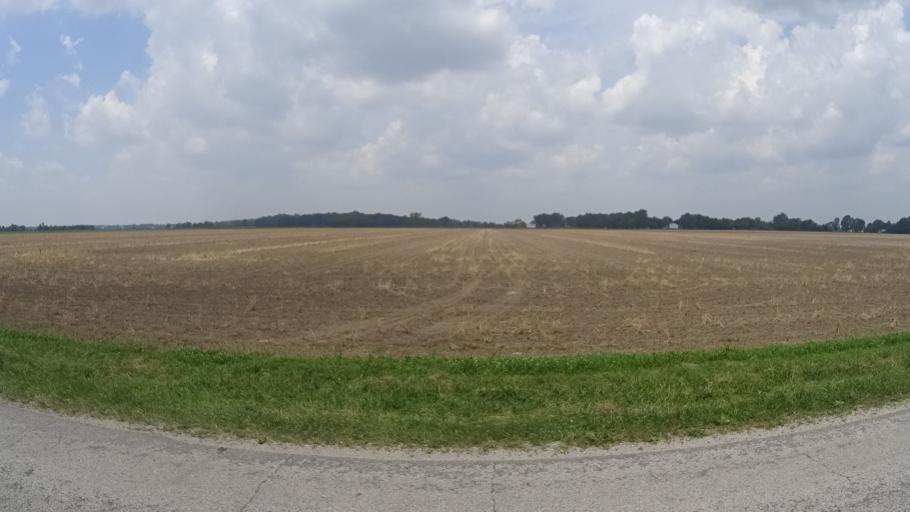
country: US
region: Ohio
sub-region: Huron County
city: Monroeville
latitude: 41.3059
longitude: -82.6926
